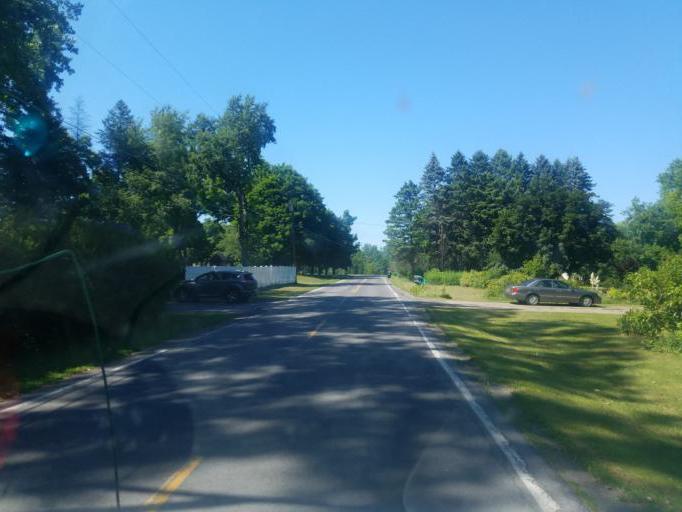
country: US
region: New York
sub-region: Ontario County
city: Phelps
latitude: 42.9315
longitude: -76.9993
